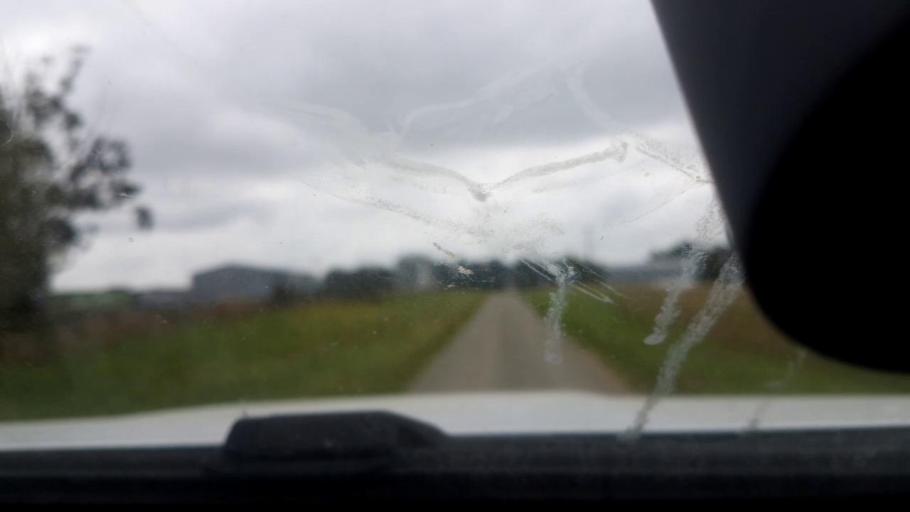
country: NZ
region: Canterbury
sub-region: Timaru District
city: Pleasant Point
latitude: -44.2257
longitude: 171.1645
